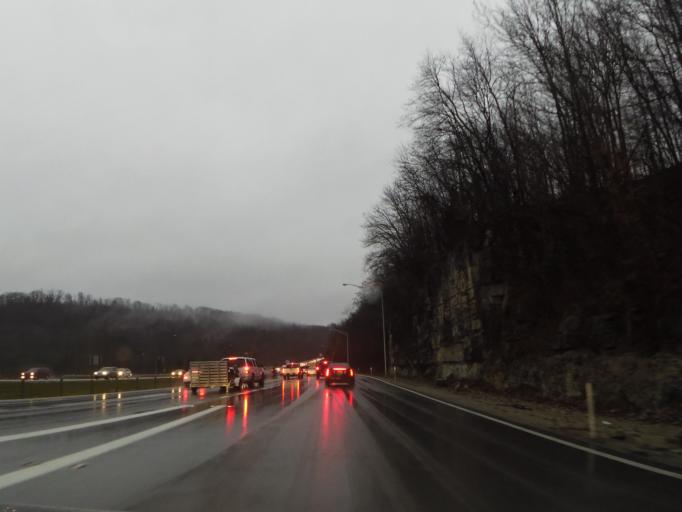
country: US
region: Kentucky
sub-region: Rockcastle County
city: Mount Vernon
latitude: 37.3398
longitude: -84.3076
